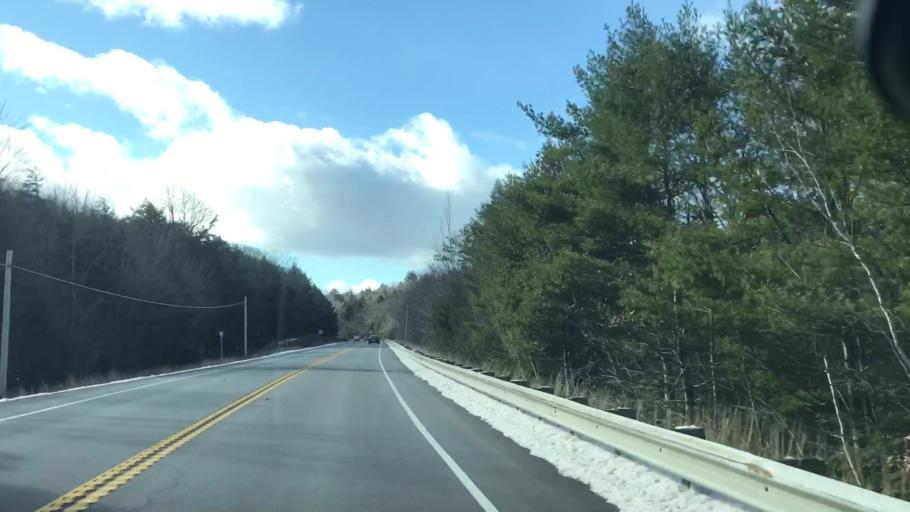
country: US
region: New Hampshire
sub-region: Carroll County
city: Ossipee
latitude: 43.6733
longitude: -71.1300
